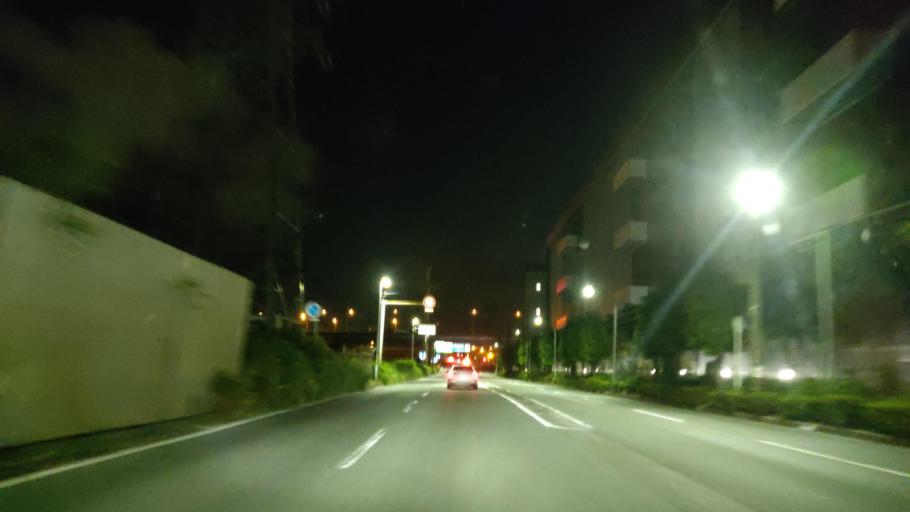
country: JP
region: Chiba
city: Funabashi
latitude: 35.6951
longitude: 139.9619
